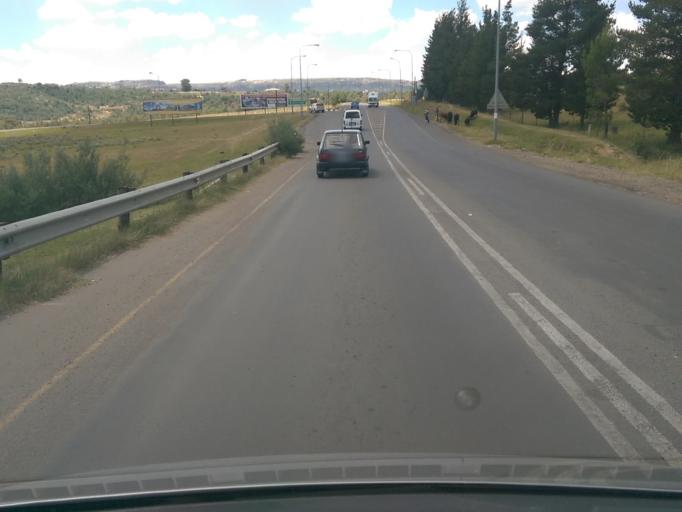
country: LS
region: Maseru
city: Maseru
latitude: -29.3924
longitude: 27.5513
